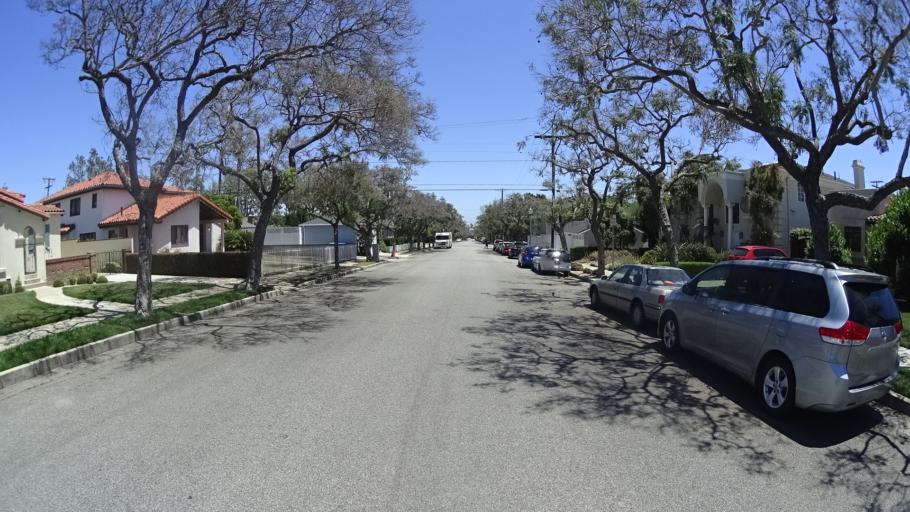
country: US
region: California
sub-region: Los Angeles County
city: Santa Monica
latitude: 34.0409
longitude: -118.4795
